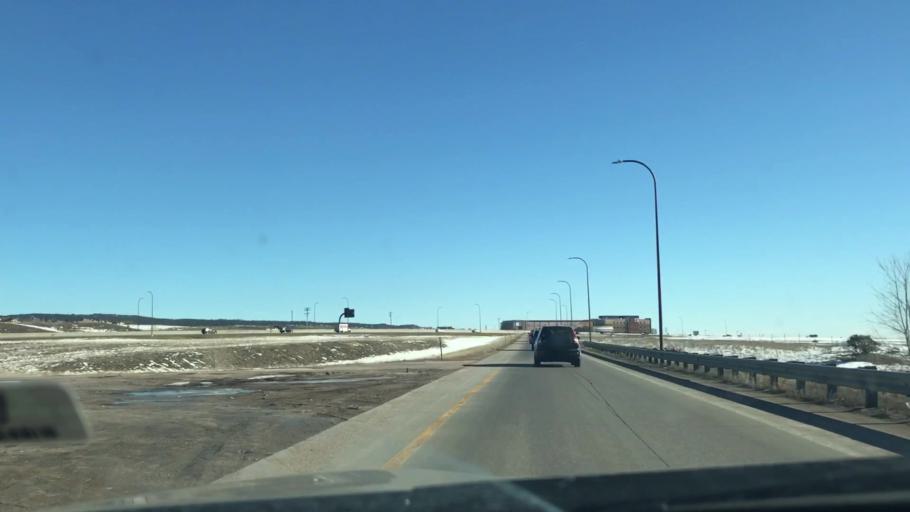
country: US
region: Colorado
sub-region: El Paso County
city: Monument
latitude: 39.0872
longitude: -104.8641
